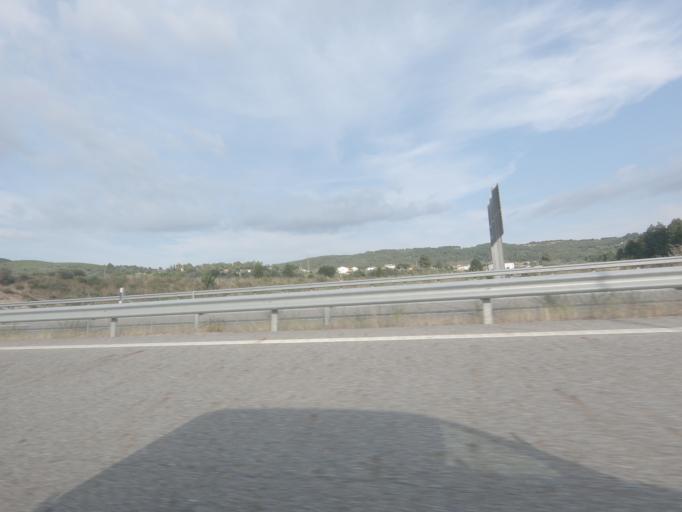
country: PT
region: Vila Real
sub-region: Boticas
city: Boticas
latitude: 41.6643
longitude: -7.5727
